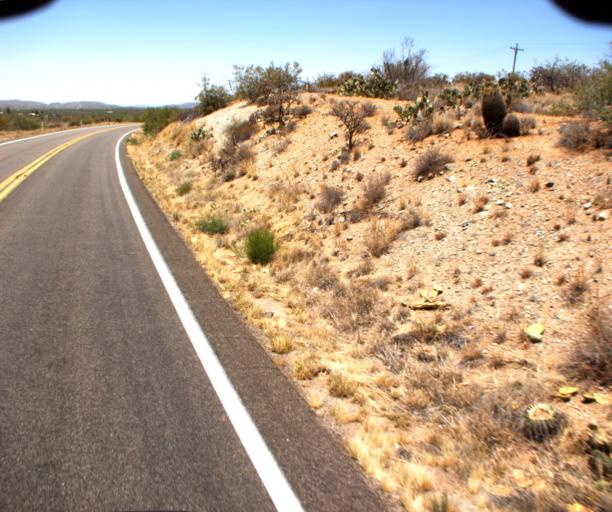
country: US
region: Arizona
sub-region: Pima County
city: Catalina
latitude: 32.6487
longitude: -111.0280
